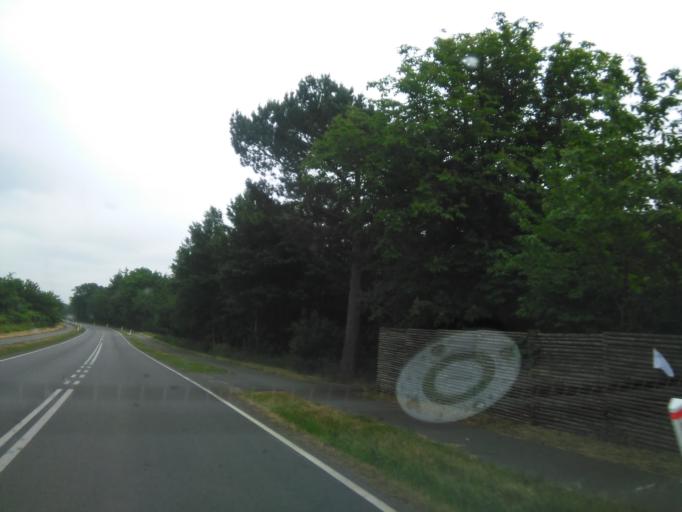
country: DK
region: Capital Region
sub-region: Bornholm Kommune
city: Ronne
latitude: 55.0512
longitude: 14.8079
